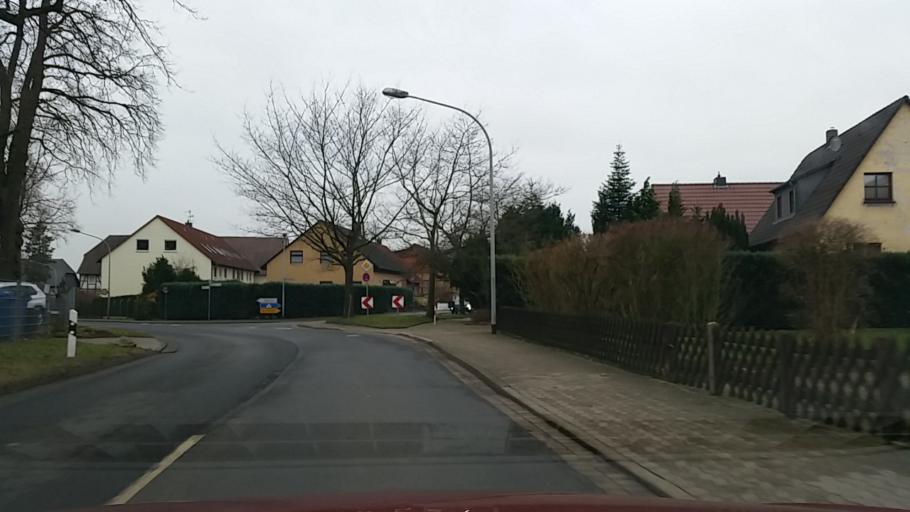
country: DE
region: Lower Saxony
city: Meine
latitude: 52.3430
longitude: 10.5793
